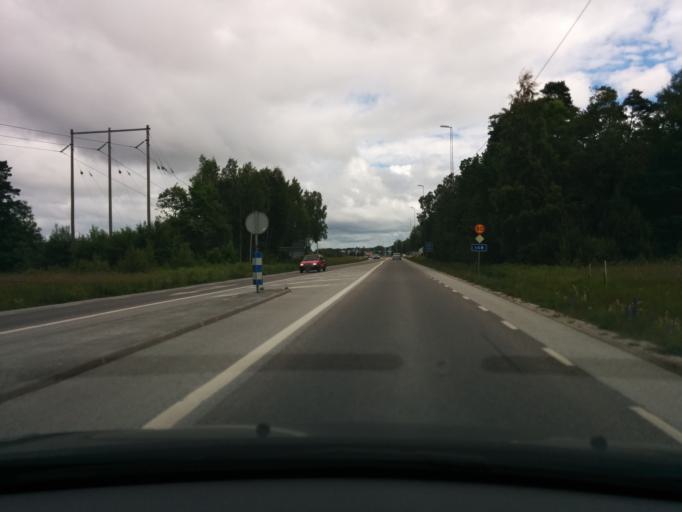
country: SE
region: Gotland
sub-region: Gotland
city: Visby
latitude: 57.6162
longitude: 18.3137
